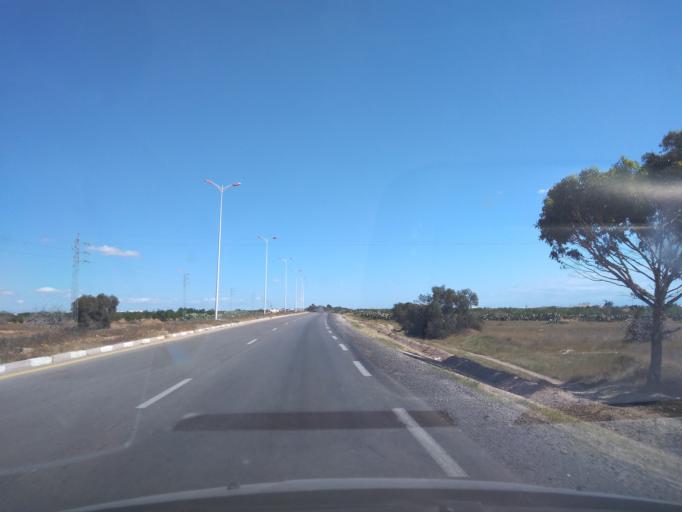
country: TN
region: Safaqis
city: Sfax
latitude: 34.8370
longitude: 10.7338
